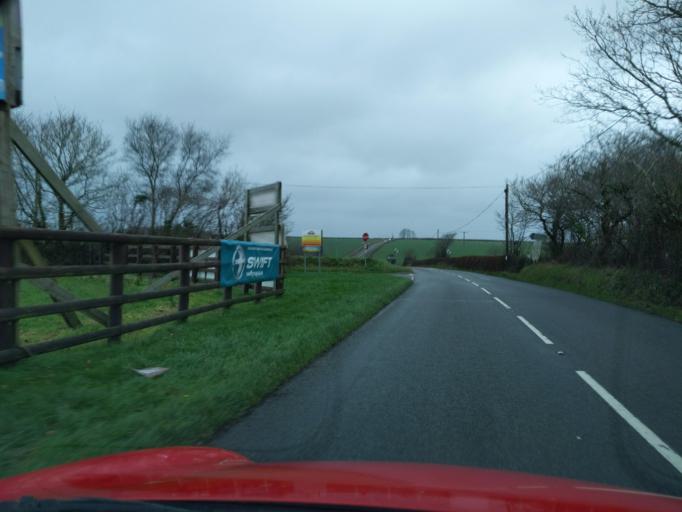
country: GB
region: England
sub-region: Cornwall
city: Boyton
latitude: 50.7155
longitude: -4.3298
